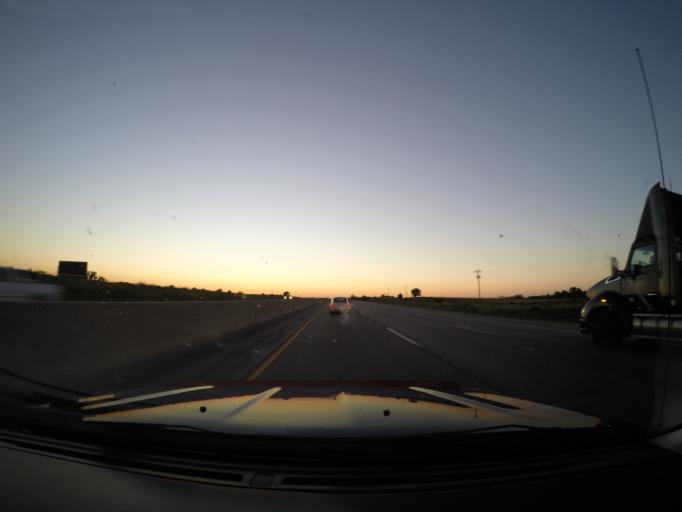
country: US
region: Kansas
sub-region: Douglas County
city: Lawrence
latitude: 39.0034
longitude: -95.4370
